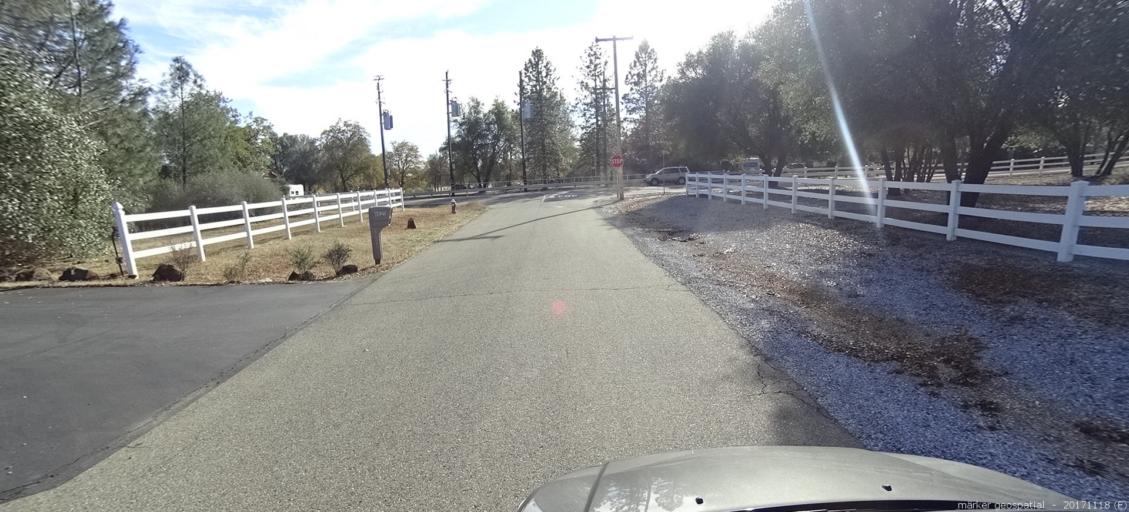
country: US
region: California
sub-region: Shasta County
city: Redding
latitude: 40.4786
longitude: -122.4334
